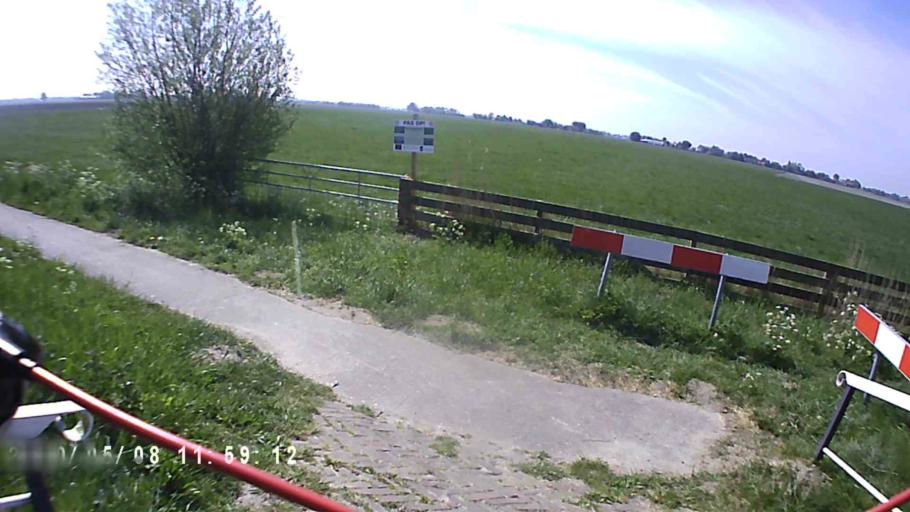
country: NL
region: Groningen
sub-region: Gemeente Bedum
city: Bedum
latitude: 53.3059
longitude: 6.6735
